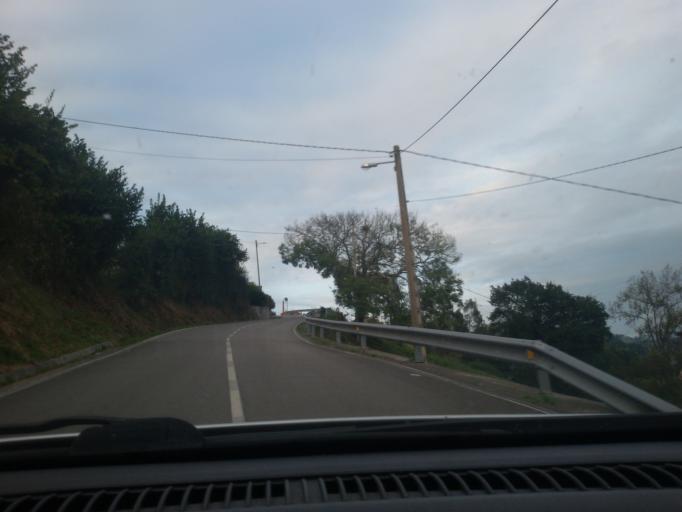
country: ES
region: Asturias
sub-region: Province of Asturias
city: Bimenes
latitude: 43.3354
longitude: -5.5862
